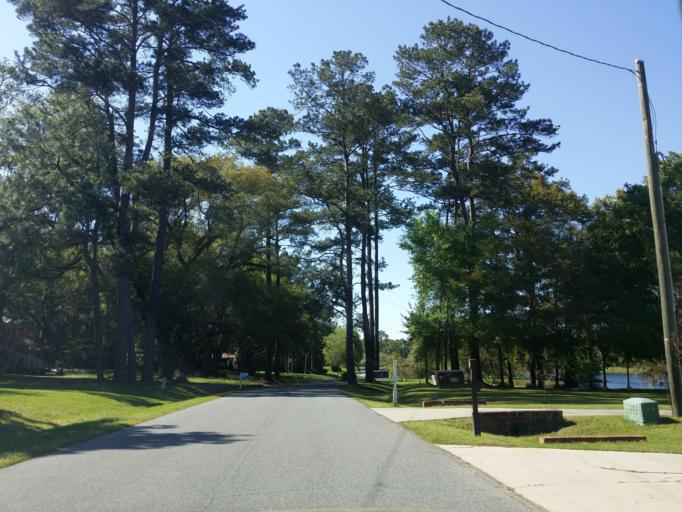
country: US
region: Florida
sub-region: Leon County
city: Tallahassee
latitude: 30.4784
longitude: -84.1876
